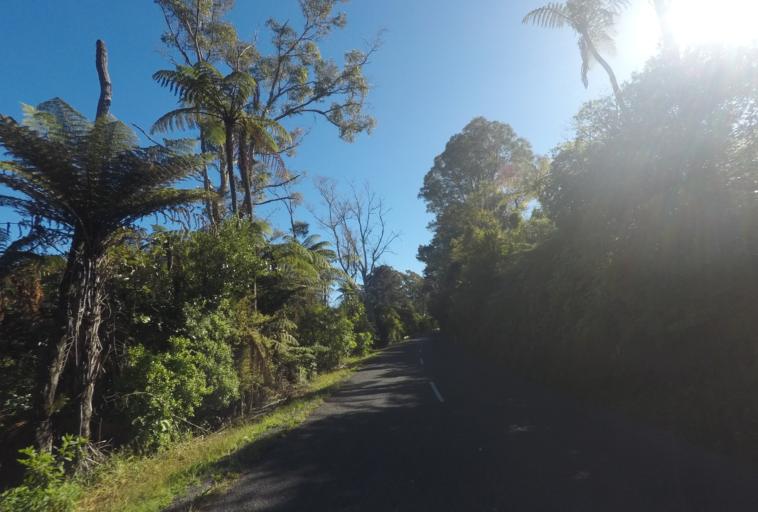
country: NZ
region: Bay of Plenty
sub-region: Western Bay of Plenty District
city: Waihi Beach
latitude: -37.3942
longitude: 175.9052
